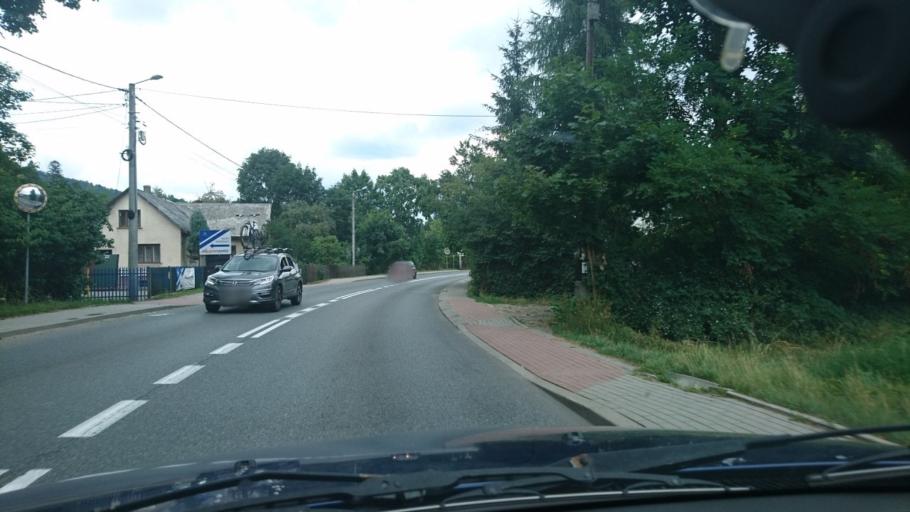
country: PL
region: Silesian Voivodeship
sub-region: Powiat zywiecki
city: Milowka
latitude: 49.5633
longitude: 19.0871
